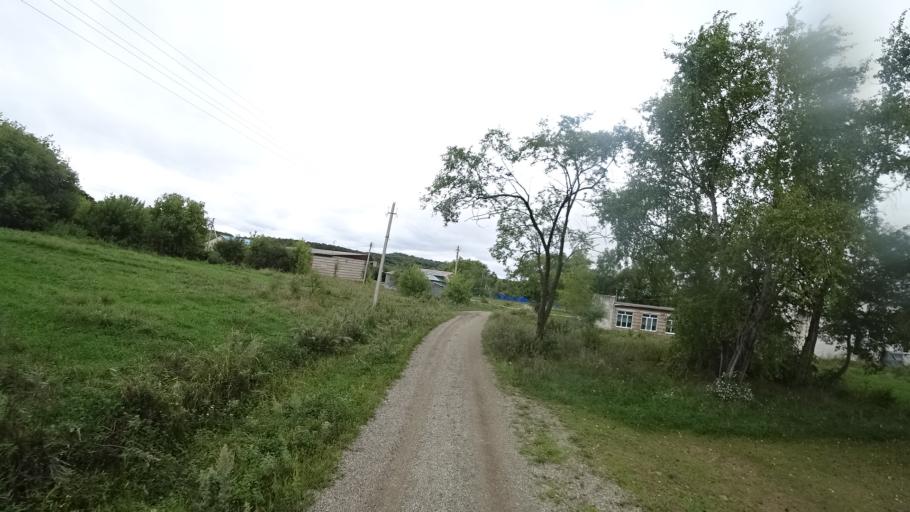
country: RU
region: Primorskiy
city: Chernigovka
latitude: 44.4583
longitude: 132.5940
